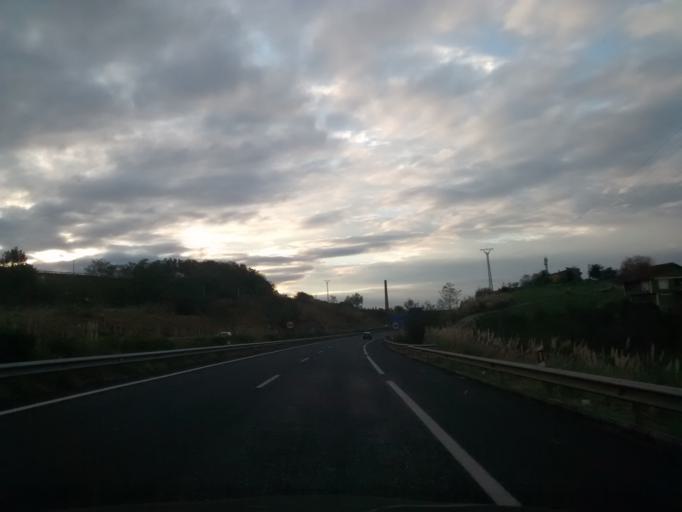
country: ES
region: Cantabria
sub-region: Provincia de Cantabria
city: Torrelavega
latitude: 43.3445
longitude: -4.0179
